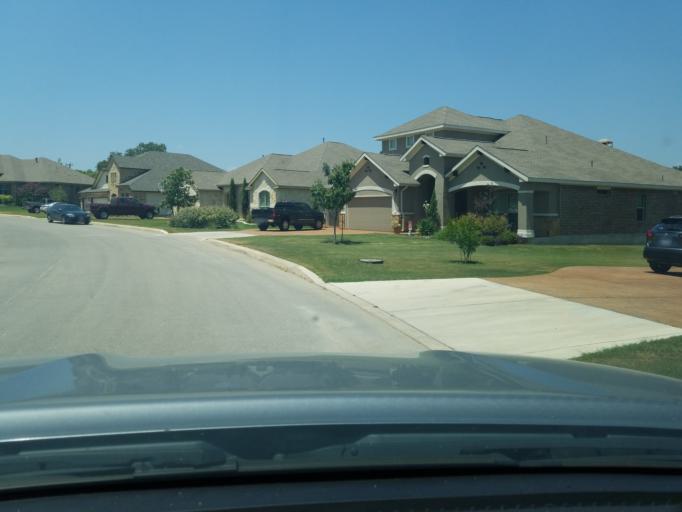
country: US
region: Texas
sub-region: Bexar County
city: Timberwood Park
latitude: 29.7103
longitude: -98.5115
